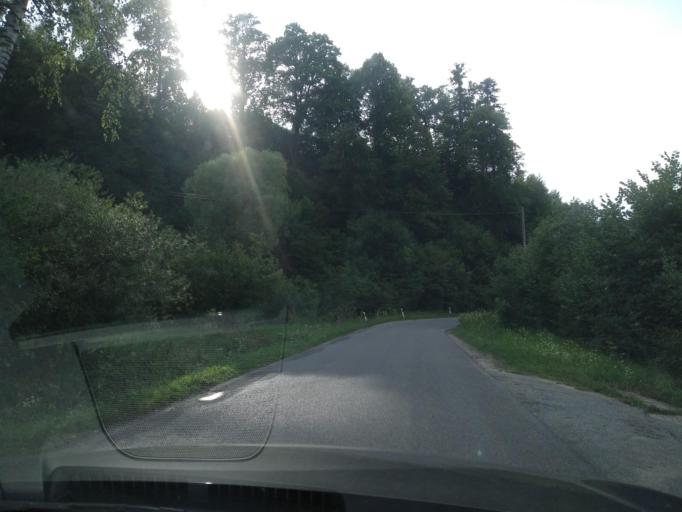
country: PL
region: Subcarpathian Voivodeship
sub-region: Powiat sanocki
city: Tyrawa Woloska
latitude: 49.5718
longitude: 22.3713
